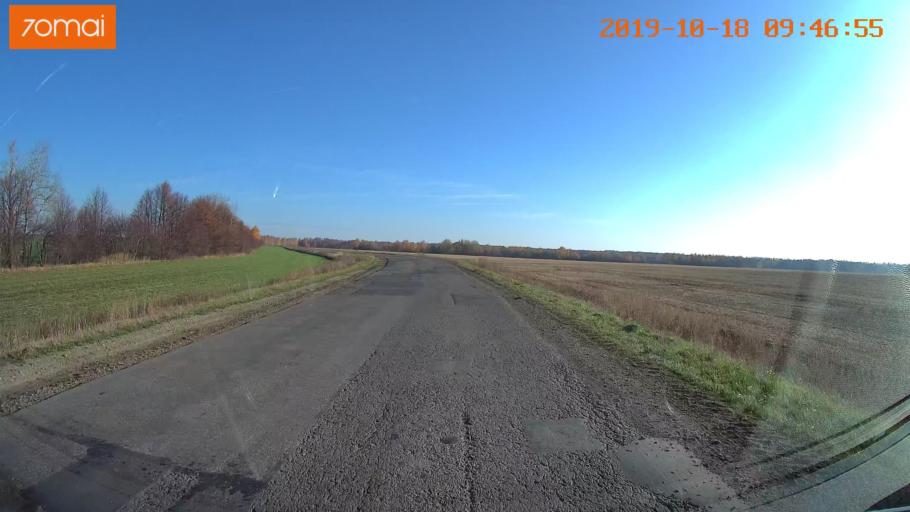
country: RU
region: Tula
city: Kazachka
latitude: 53.3149
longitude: 38.2220
